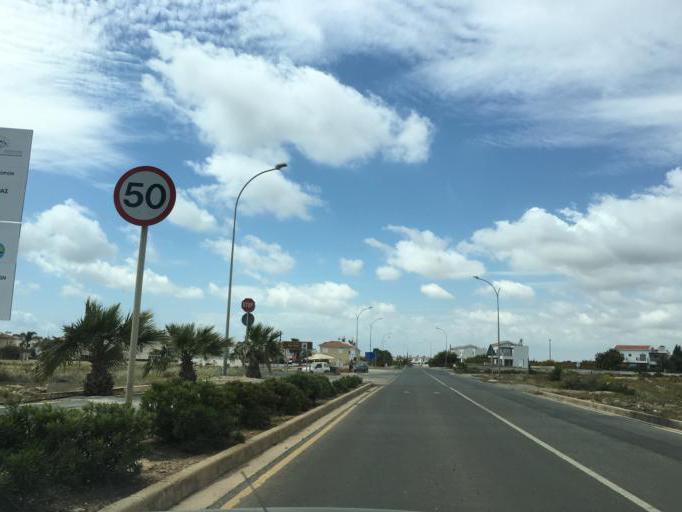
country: CY
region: Ammochostos
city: Liopetri
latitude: 34.9810
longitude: 33.9329
